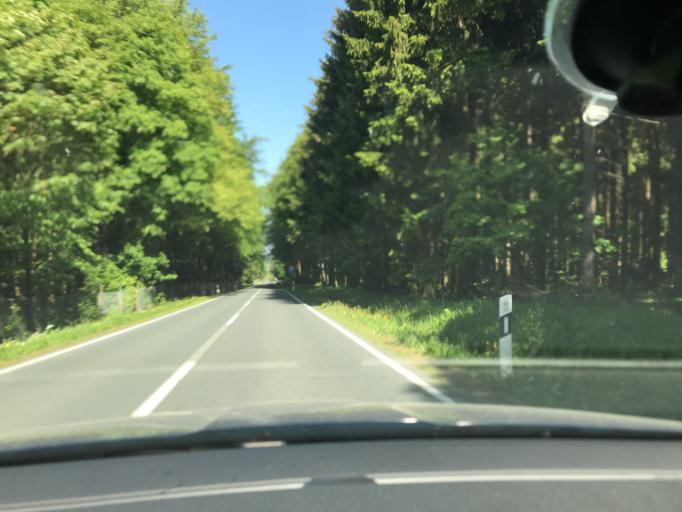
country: CZ
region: Ustecky
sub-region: Okres Chomutov
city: Vejprty
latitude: 50.4618
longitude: 12.9945
